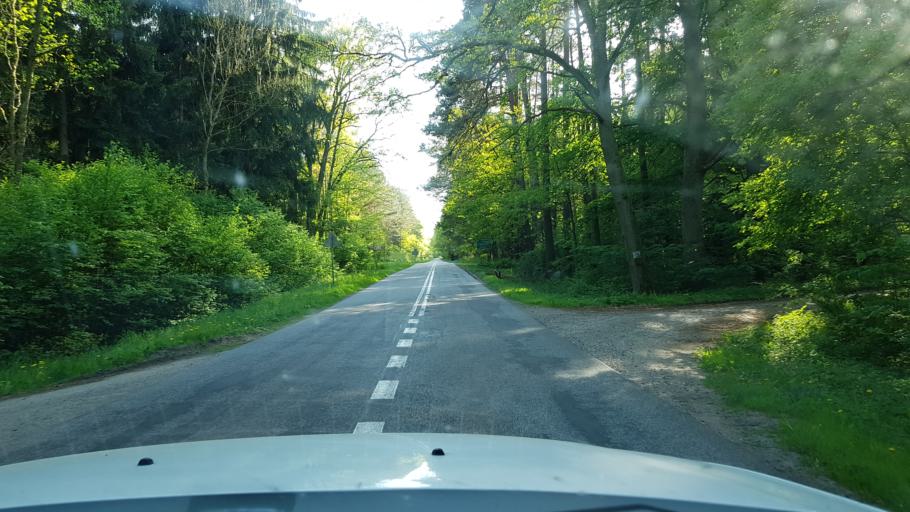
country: PL
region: West Pomeranian Voivodeship
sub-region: Powiat lobeski
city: Resko
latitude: 53.7296
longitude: 15.3268
